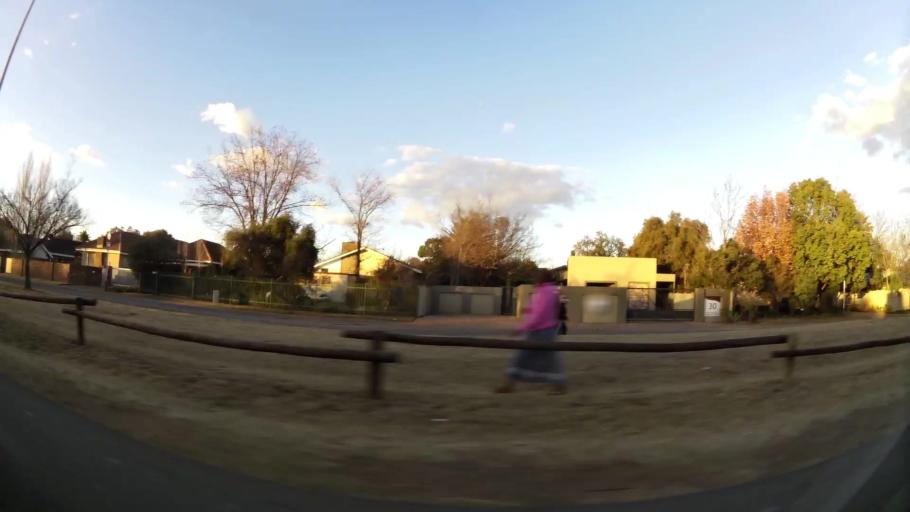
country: ZA
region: North-West
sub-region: Dr Kenneth Kaunda District Municipality
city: Potchefstroom
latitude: -26.7153
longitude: 27.1130
